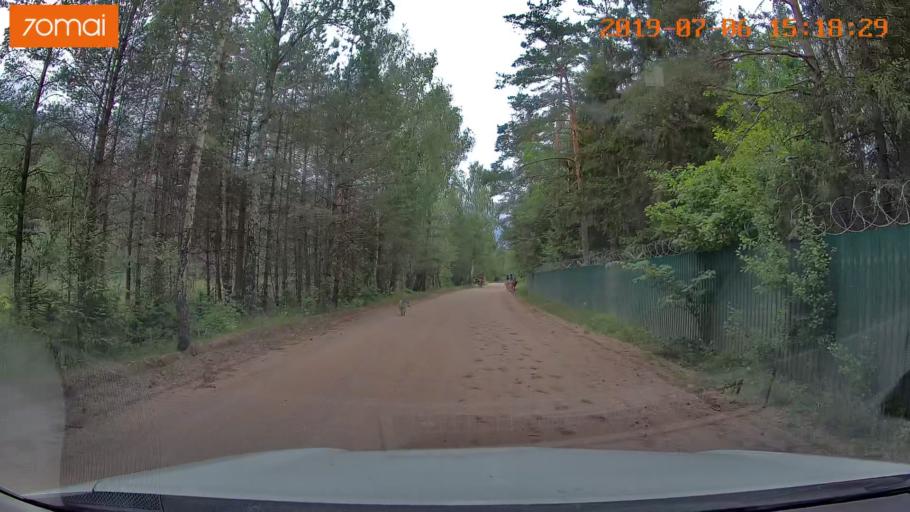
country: BY
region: Minsk
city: Ivyanyets
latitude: 53.9927
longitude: 26.6526
